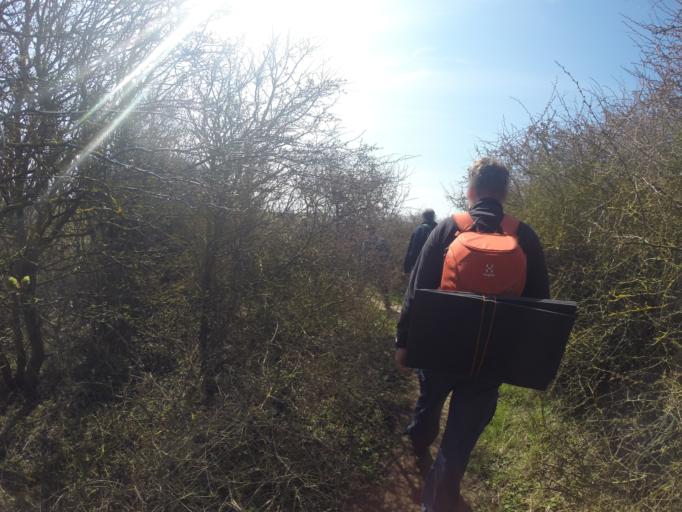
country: DK
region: Zealand
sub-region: Kalundborg Kommune
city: Gorlev
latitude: 55.5232
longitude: 11.0847
